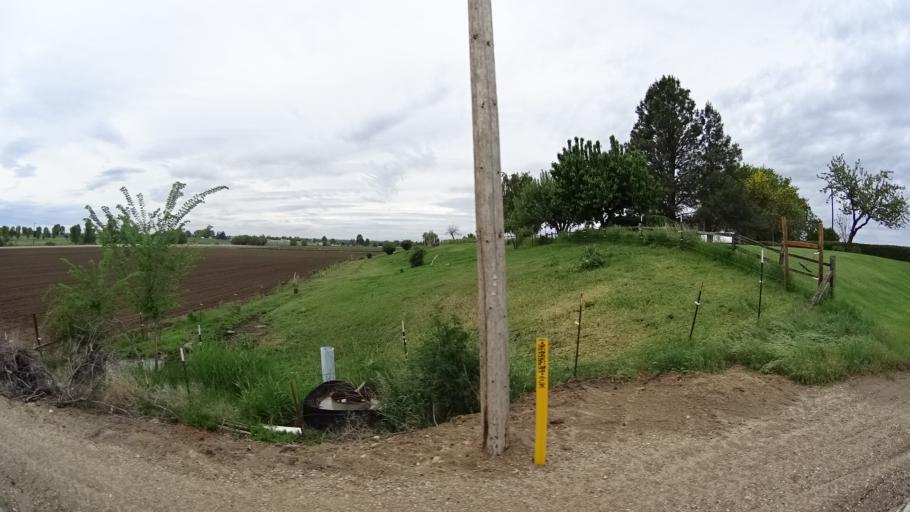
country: US
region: Idaho
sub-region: Ada County
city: Star
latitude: 43.7212
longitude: -116.4704
